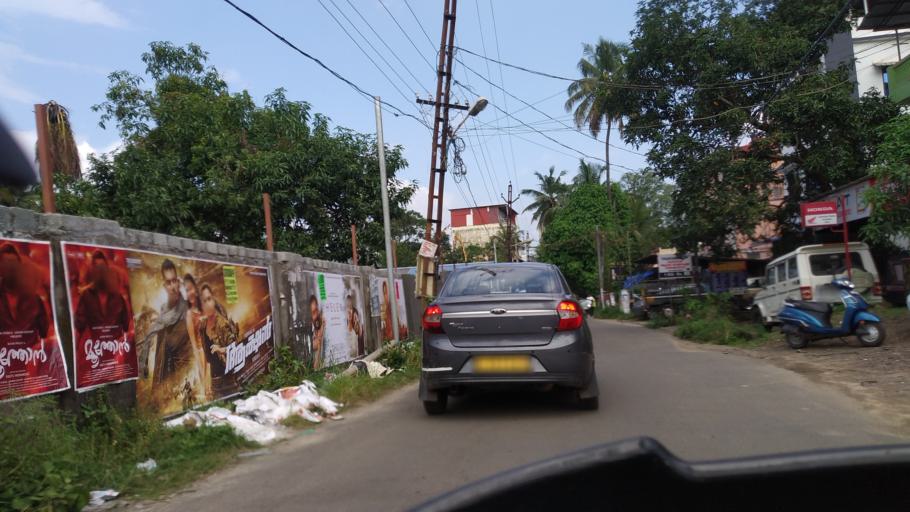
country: IN
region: Kerala
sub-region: Ernakulam
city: Cochin
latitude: 9.9833
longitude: 76.2939
